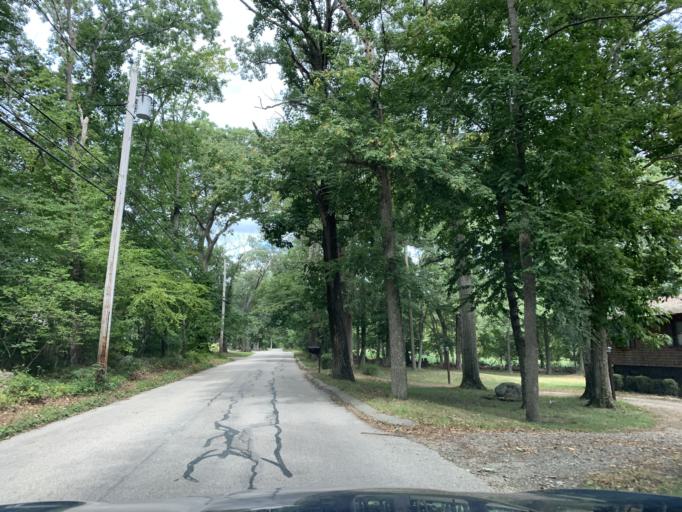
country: US
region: Rhode Island
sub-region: Washington County
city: Exeter
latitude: 41.5558
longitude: -71.6217
